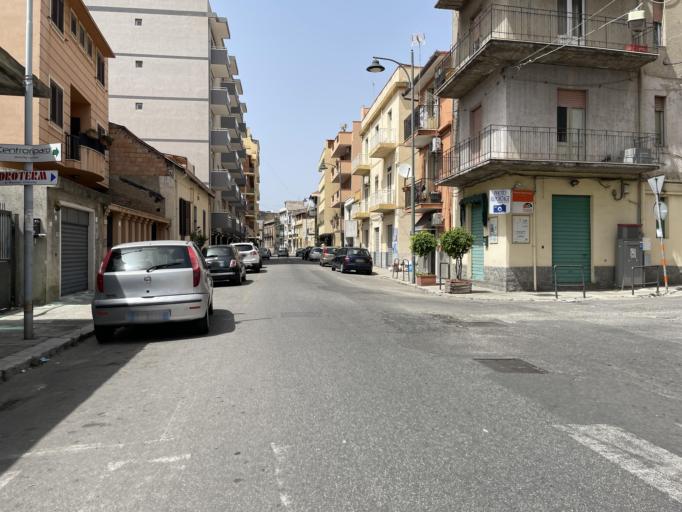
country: IT
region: Calabria
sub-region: Provincia di Reggio Calabria
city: Reggio Calabria
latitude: 38.0958
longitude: 15.6433
